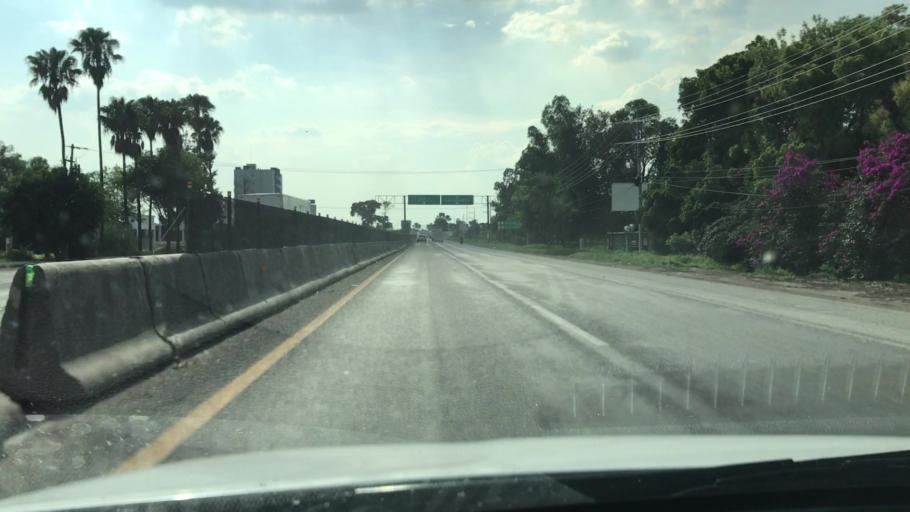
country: MX
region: Guanajuato
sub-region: Salamanca
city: El Divisador
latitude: 20.5561
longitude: -101.1592
